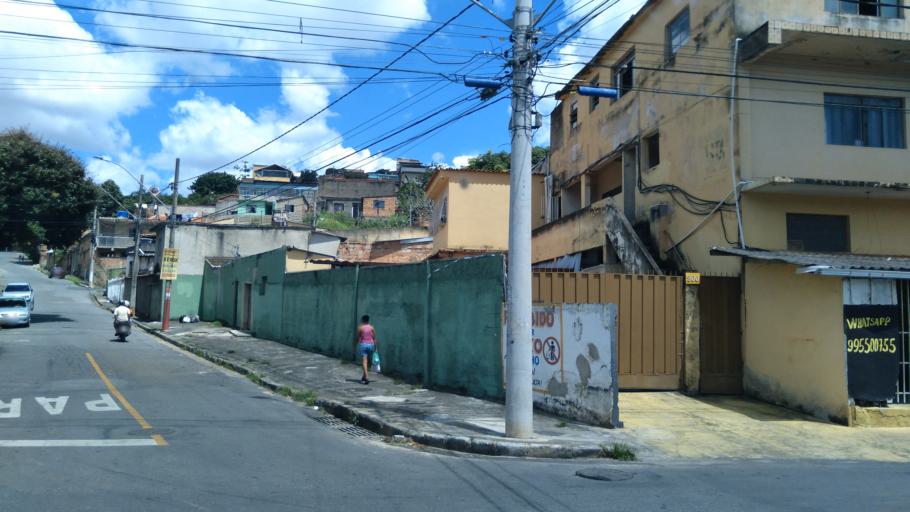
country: BR
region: Minas Gerais
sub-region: Belo Horizonte
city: Belo Horizonte
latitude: -19.8697
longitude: -43.9119
